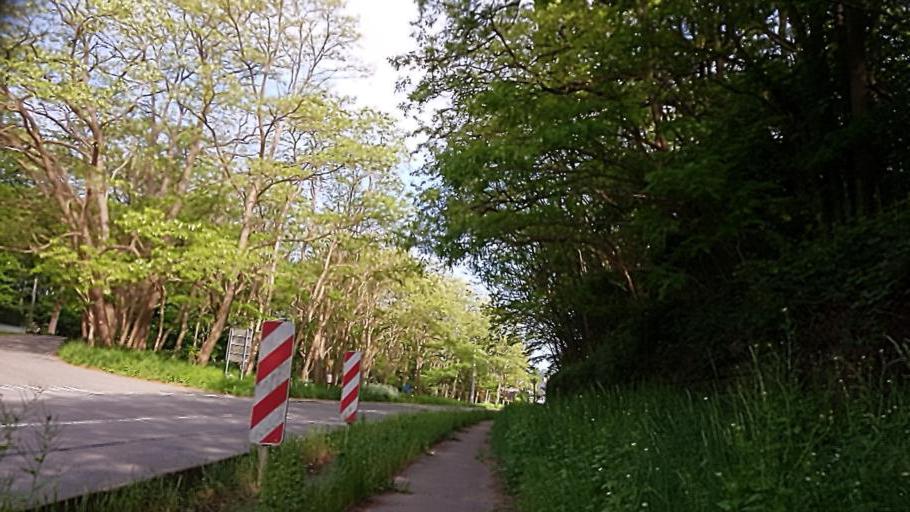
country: BE
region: Wallonia
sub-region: Province du Brabant Wallon
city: Wavre
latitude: 50.7464
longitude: 4.5724
